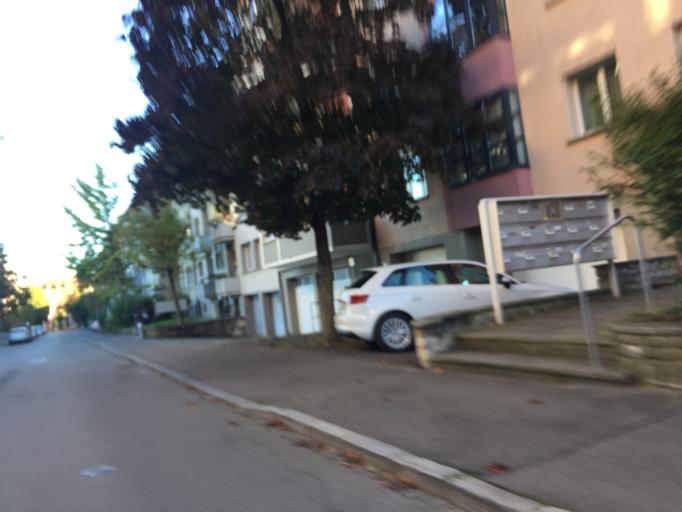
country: CH
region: Bern
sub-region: Bern-Mittelland District
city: Bern
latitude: 46.9423
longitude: 7.4275
